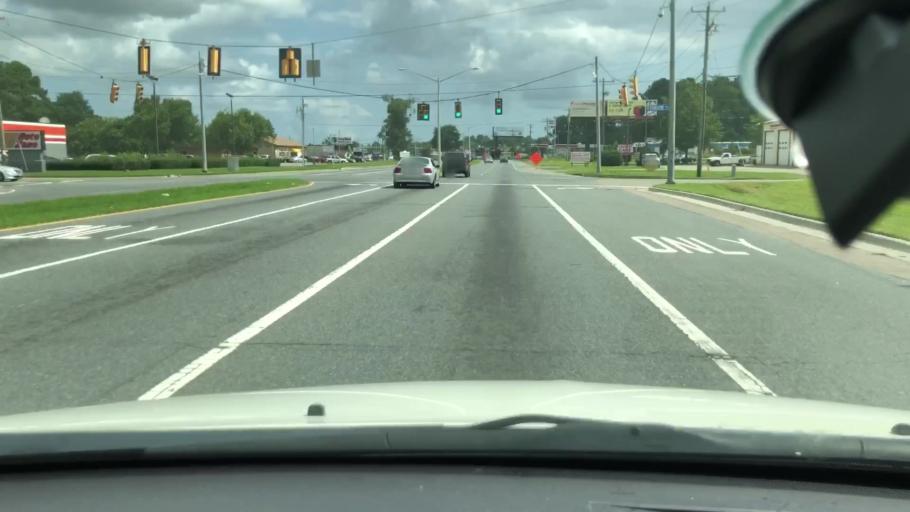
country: US
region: Virginia
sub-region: City of Chesapeake
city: Chesapeake
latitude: 36.8060
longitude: -76.2226
